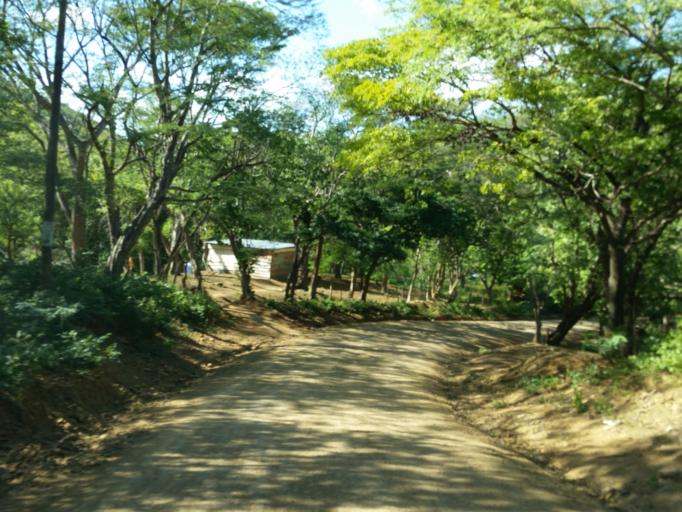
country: NI
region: Rivas
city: San Juan del Sur
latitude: 11.1859
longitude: -85.8007
